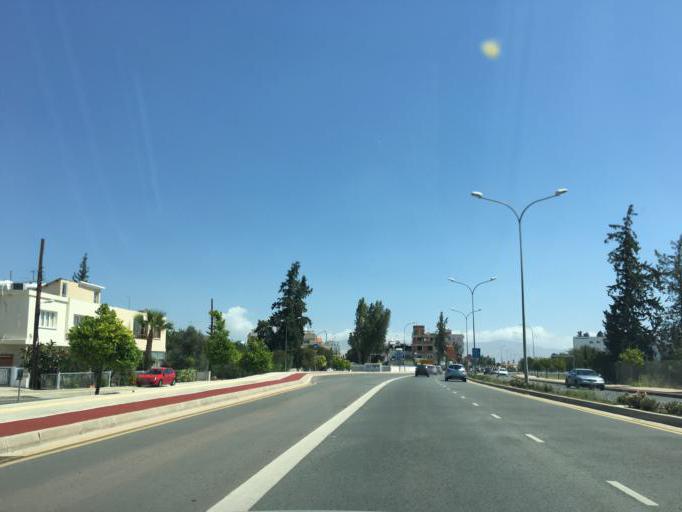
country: CY
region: Lefkosia
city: Nicosia
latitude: 35.1511
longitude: 33.3275
